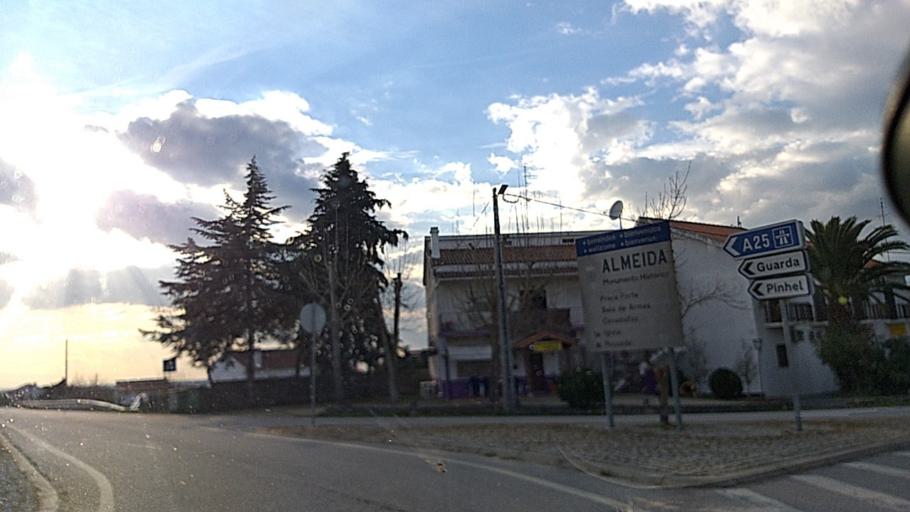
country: ES
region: Castille and Leon
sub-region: Provincia de Salamanca
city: Aldea del Obispo
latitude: 40.7203
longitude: -6.9023
